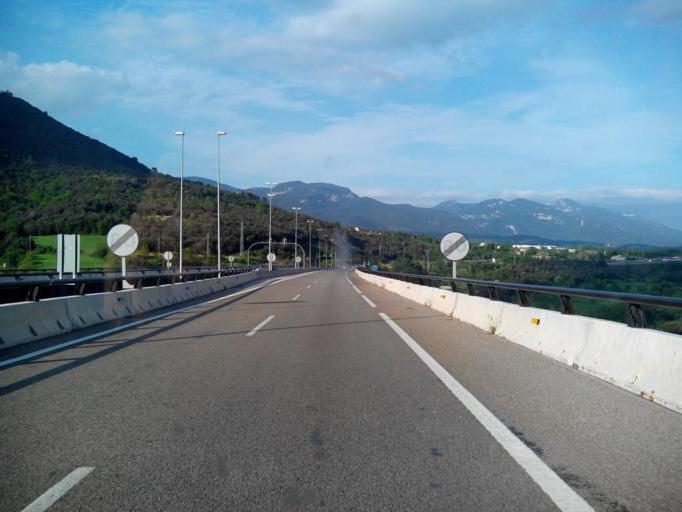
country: ES
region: Catalonia
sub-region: Provincia de Girona
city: Sant Joan les Fonts
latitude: 42.2156
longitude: 2.5450
